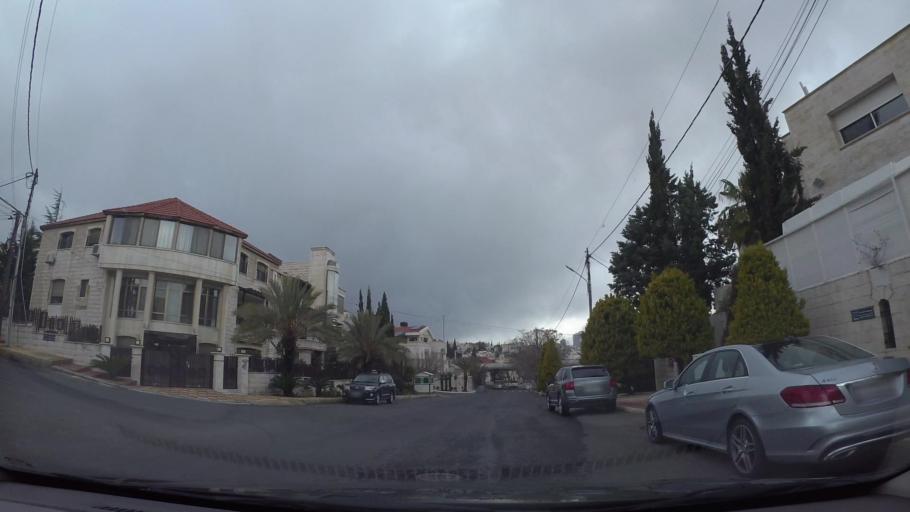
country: JO
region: Amman
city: Amman
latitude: 31.9500
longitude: 35.8946
